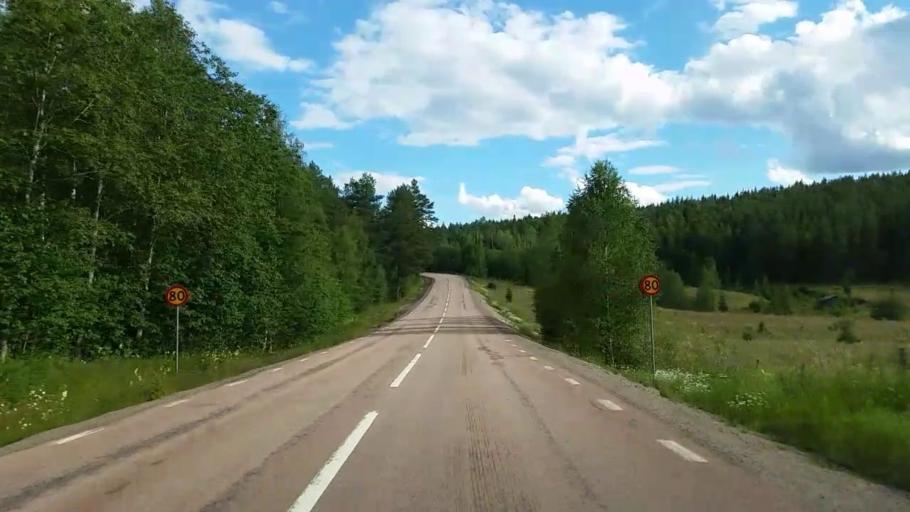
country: SE
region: Gaevleborg
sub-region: Ljusdals Kommun
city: Farila
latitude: 61.8941
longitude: 15.9080
